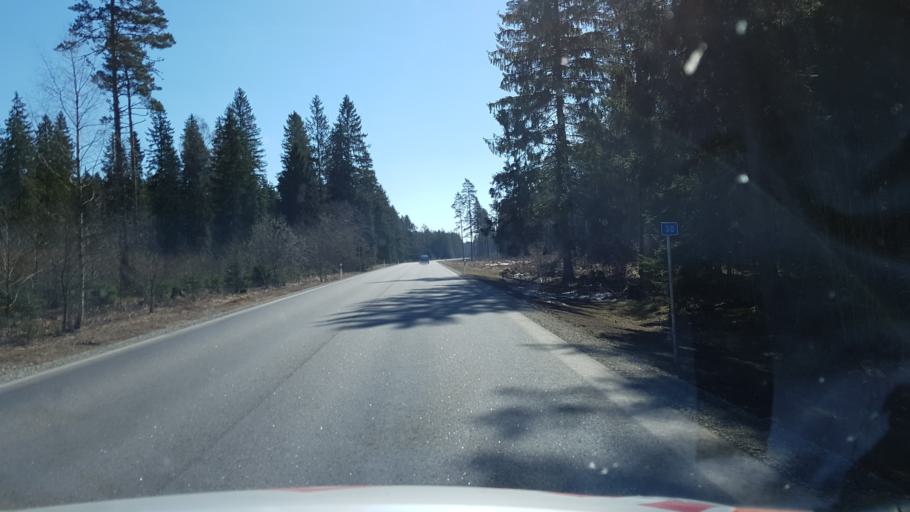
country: EE
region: Laeaene-Virumaa
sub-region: Vinni vald
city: Vinni
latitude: 59.1330
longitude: 26.6024
